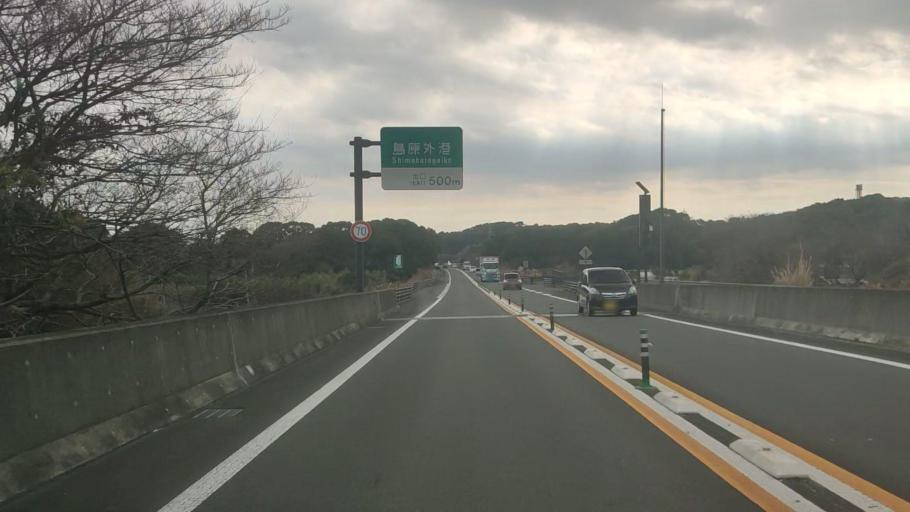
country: JP
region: Nagasaki
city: Shimabara
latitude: 32.7677
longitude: 130.3592
